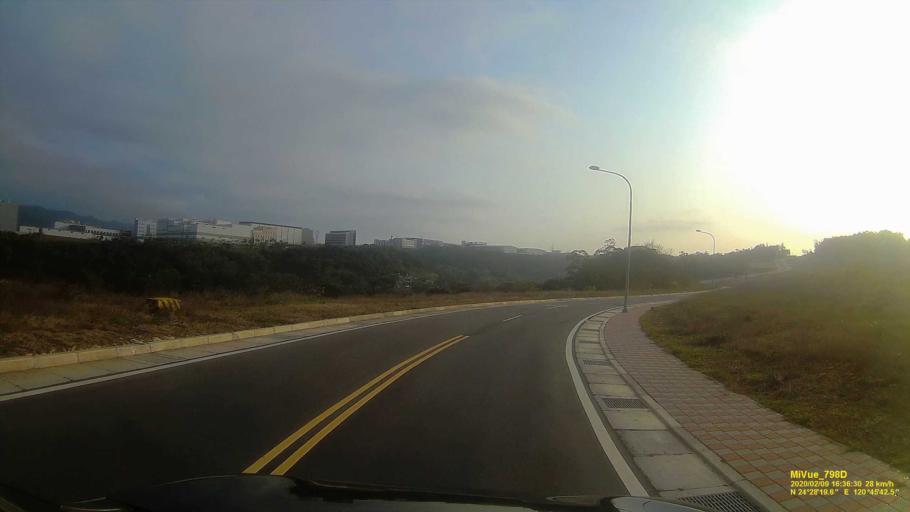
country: TW
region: Taiwan
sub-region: Miaoli
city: Miaoli
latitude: 24.4720
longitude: 120.7617
